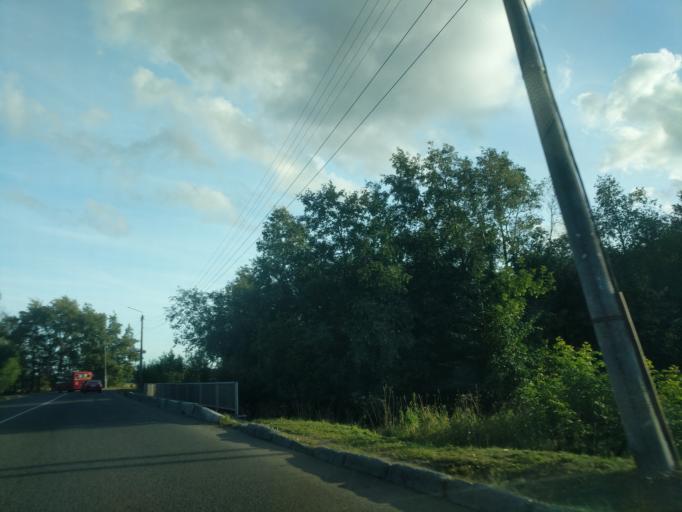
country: RU
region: Kirov
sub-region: Kirovo-Chepetskiy Rayon
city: Kirov
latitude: 58.6158
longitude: 49.7674
